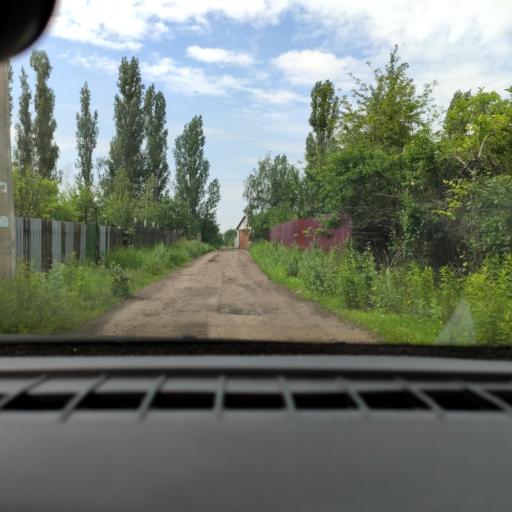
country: RU
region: Voronezj
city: Maslovka
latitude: 51.5017
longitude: 39.1984
